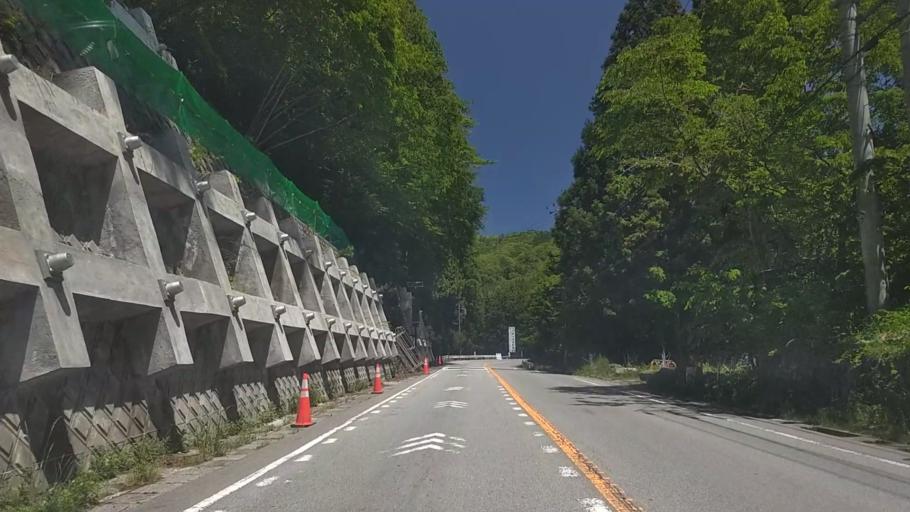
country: JP
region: Yamanashi
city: Nirasaki
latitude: 35.8835
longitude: 138.4264
